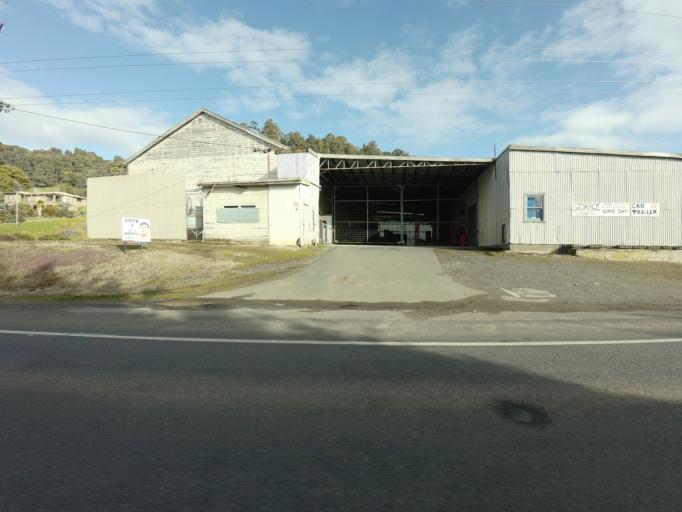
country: AU
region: Tasmania
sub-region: Huon Valley
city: Franklin
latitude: -43.0974
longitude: 147.0061
